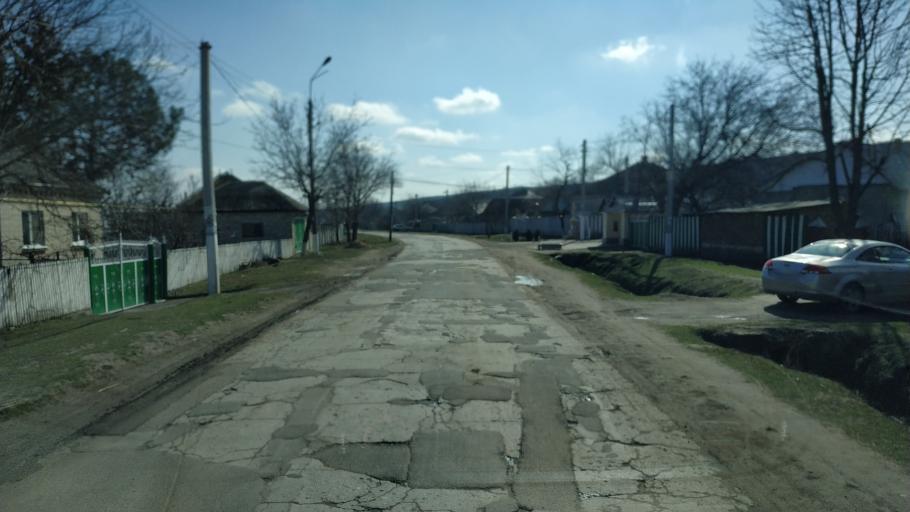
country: MD
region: Hincesti
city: Hincesti
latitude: 46.9557
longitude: 28.6065
